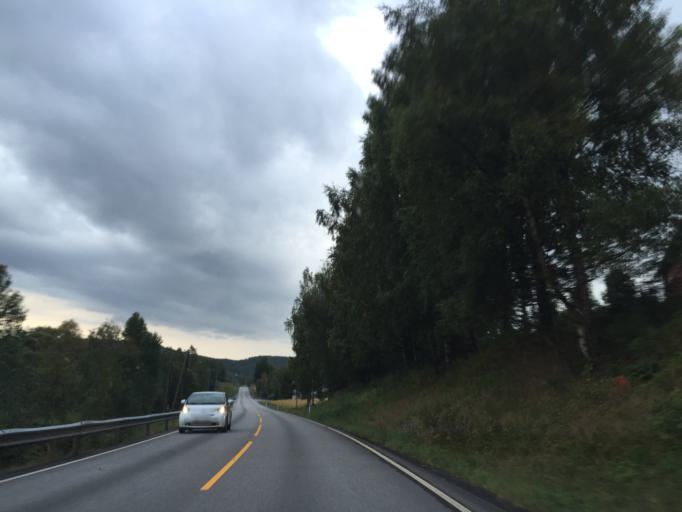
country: NO
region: Hedmark
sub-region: Nord-Odal
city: Sand
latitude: 60.4419
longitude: 11.4989
